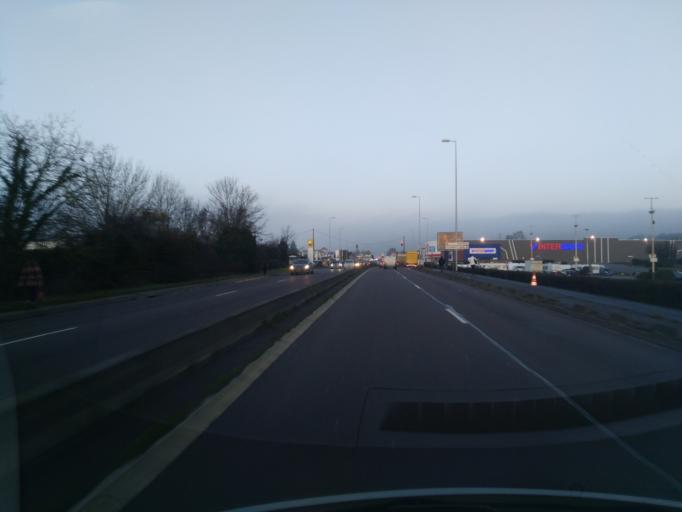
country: FR
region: Ile-de-France
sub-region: Departement des Yvelines
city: Orgeval
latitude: 48.9262
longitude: 1.9889
